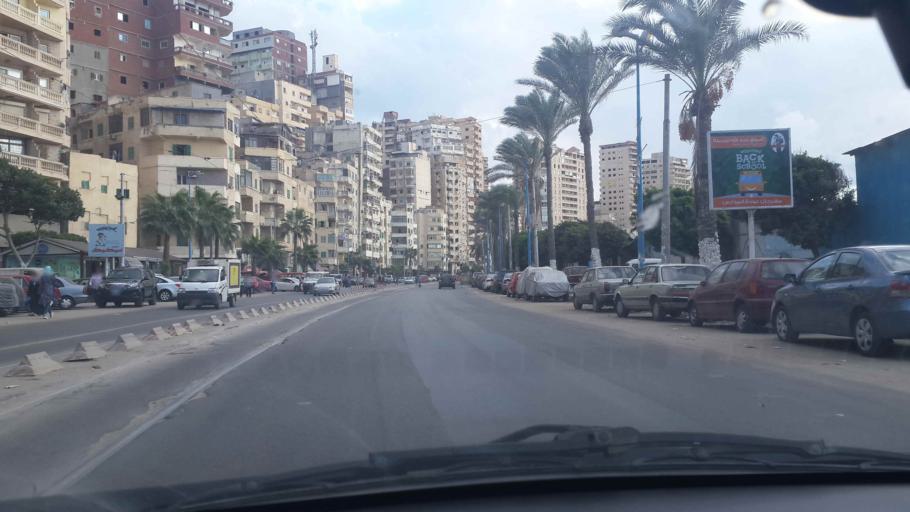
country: EG
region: Alexandria
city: Alexandria
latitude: 31.2083
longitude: 29.8792
